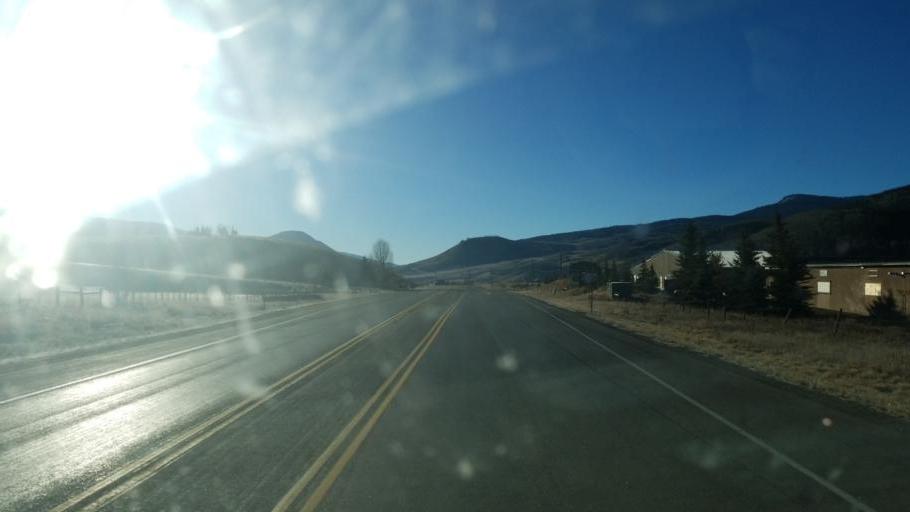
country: US
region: Colorado
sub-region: Gunnison County
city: Crested Butte
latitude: 38.8437
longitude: -106.9430
